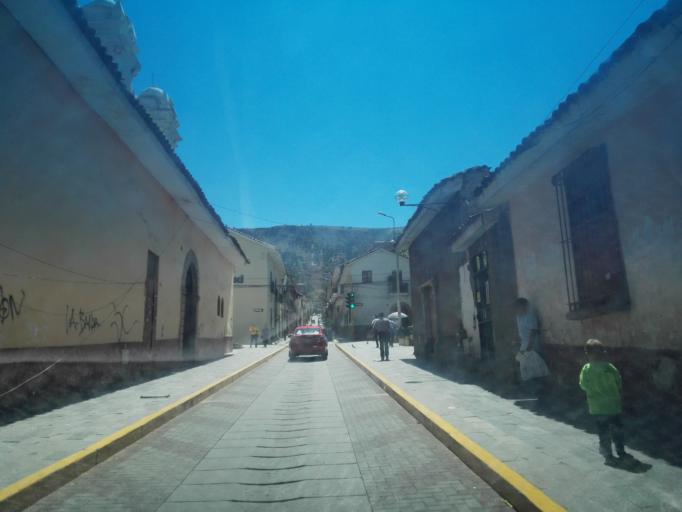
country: PE
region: Ayacucho
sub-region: Provincia de Huamanga
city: Ayacucho
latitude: -13.1595
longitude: -74.2270
